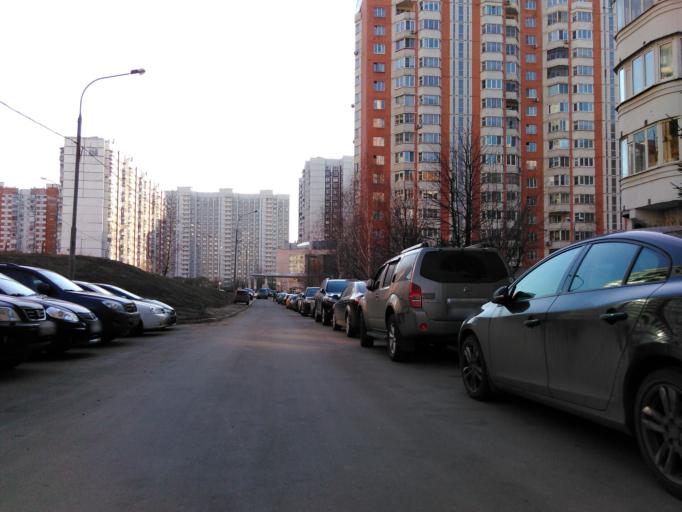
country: RU
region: Moscow
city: Ramenki
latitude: 55.6984
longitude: 37.5050
